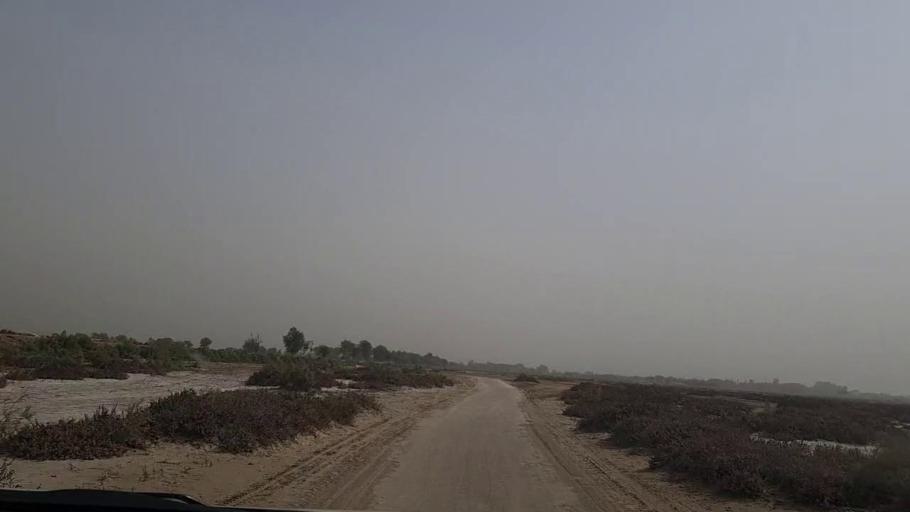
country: PK
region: Sindh
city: Pithoro
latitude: 25.4676
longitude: 69.2729
